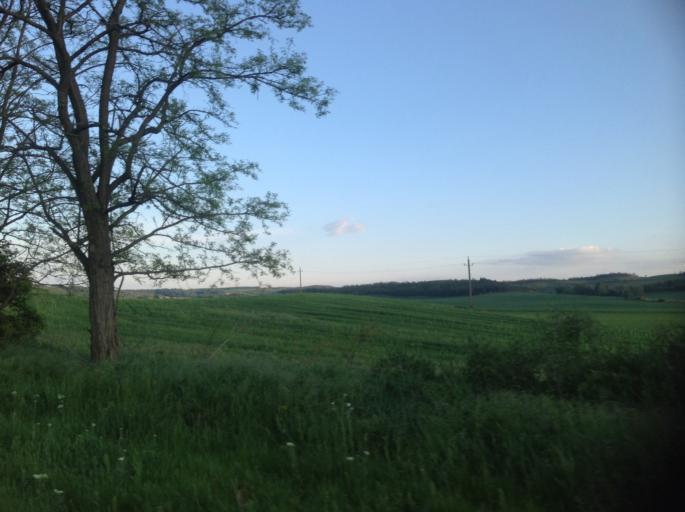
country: HU
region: Komarom-Esztergom
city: Sarisap
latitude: 47.6579
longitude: 18.7034
